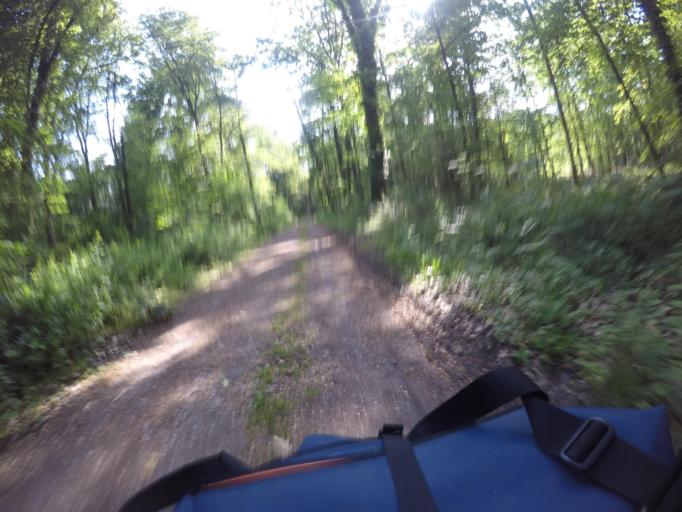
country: DE
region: Baden-Wuerttemberg
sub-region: Karlsruhe Region
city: Ettlingen
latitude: 48.9588
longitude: 8.3672
